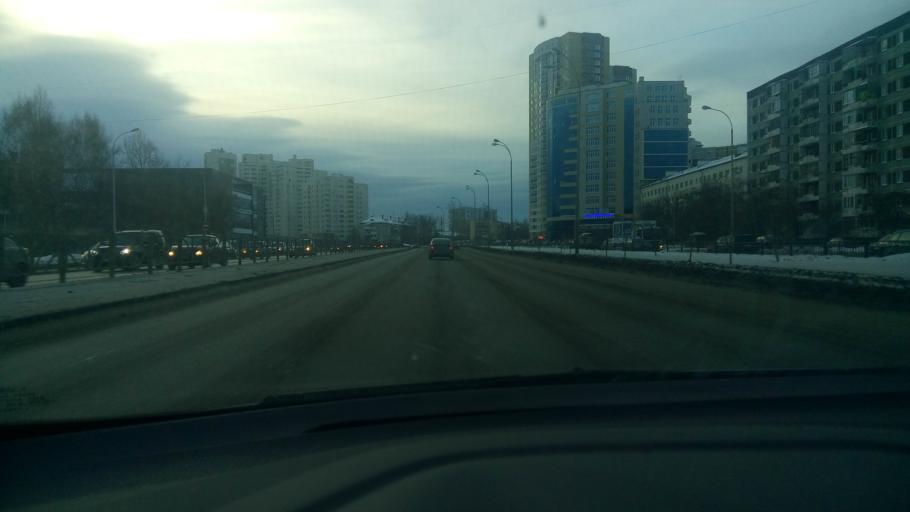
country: RU
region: Sverdlovsk
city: Yekaterinburg
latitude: 56.8071
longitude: 60.6309
